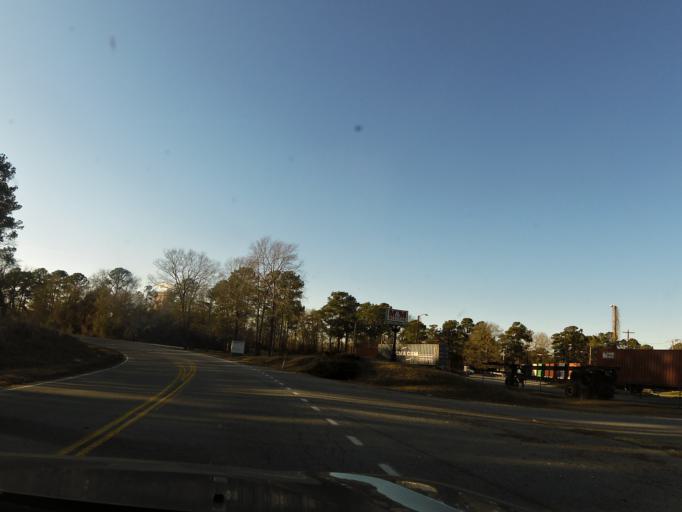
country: US
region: Virginia
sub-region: City of Franklin
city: Franklin
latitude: 36.6779
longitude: -76.9033
